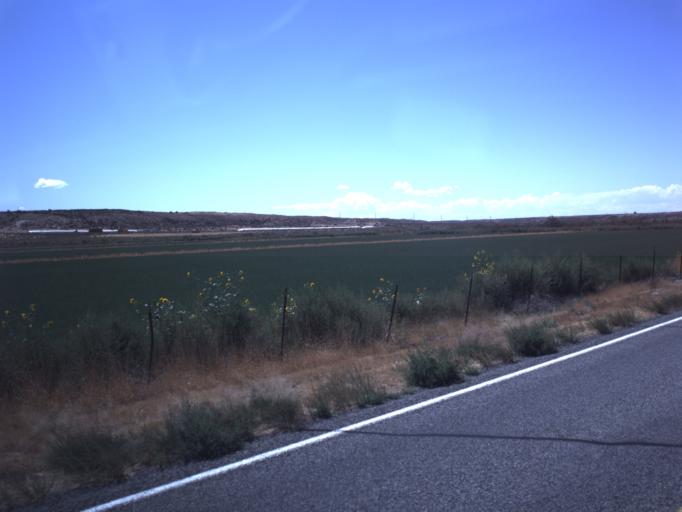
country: US
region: Utah
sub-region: Millard County
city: Delta
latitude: 39.5316
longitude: -112.3351
